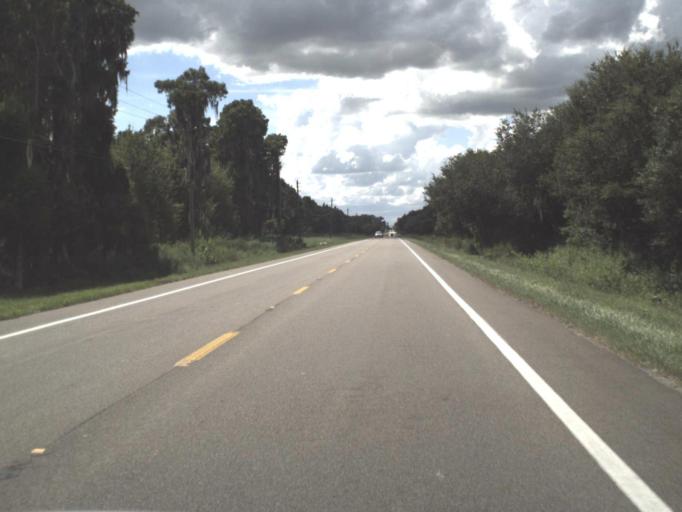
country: US
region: Florida
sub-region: Polk County
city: Highland City
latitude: 27.9968
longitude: -81.8735
